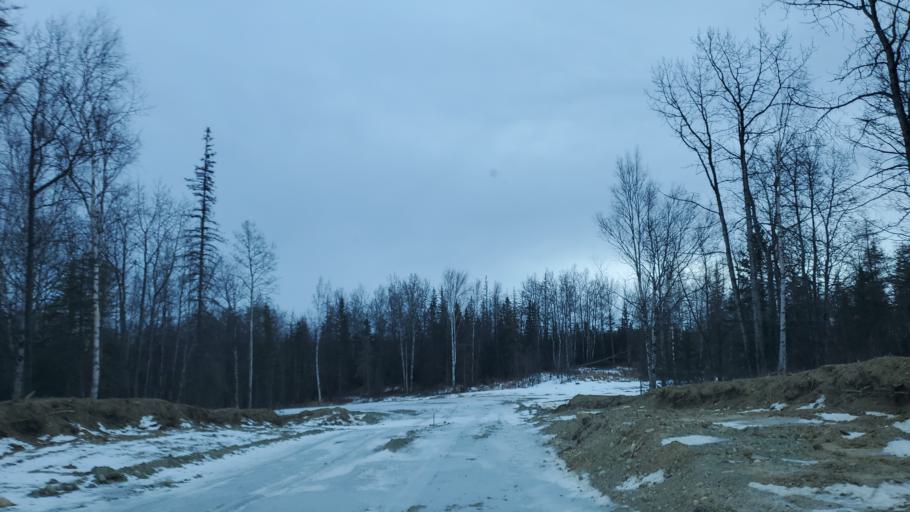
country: US
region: Alaska
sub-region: Matanuska-Susitna Borough
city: Gateway
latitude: 61.6540
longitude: -149.2346
